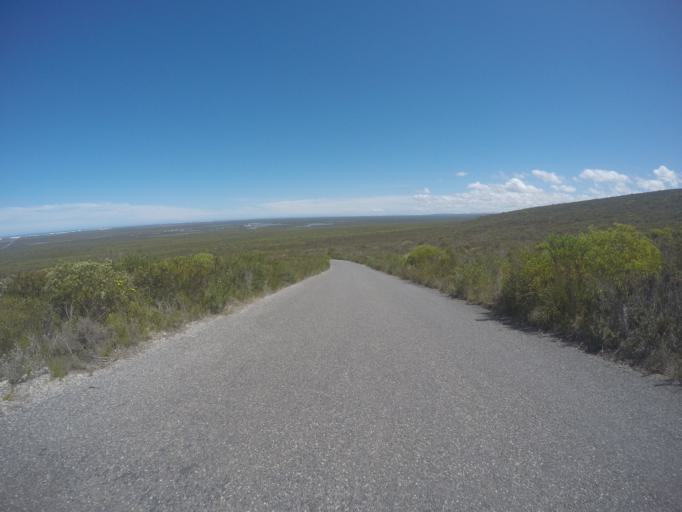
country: ZA
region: Western Cape
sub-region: Overberg District Municipality
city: Bredasdorp
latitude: -34.4274
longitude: 20.4148
